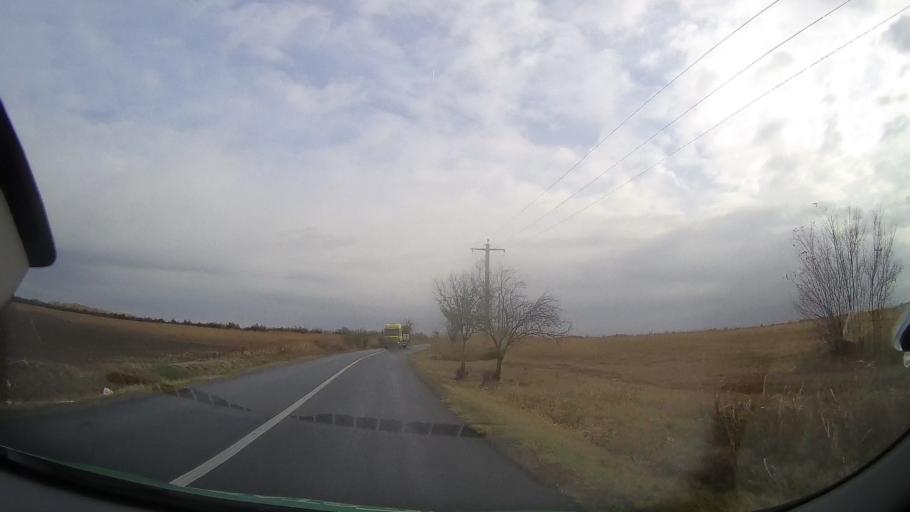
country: RO
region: Ialomita
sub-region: Comuna Maia
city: Maia
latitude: 44.7540
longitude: 26.3843
